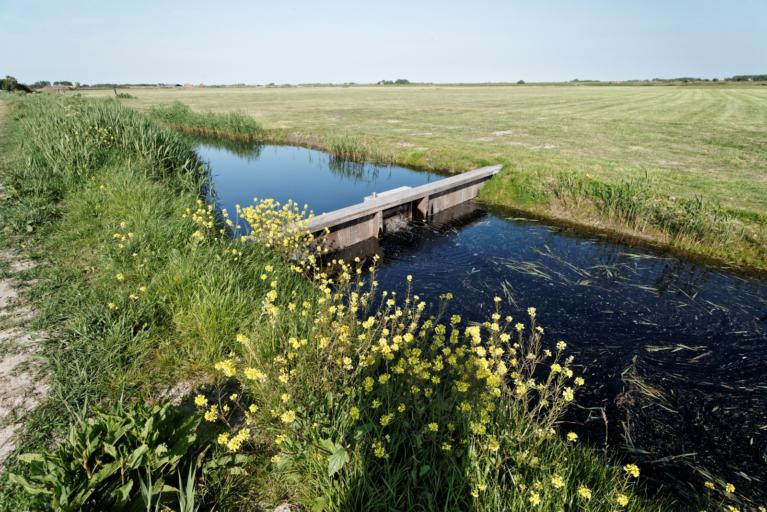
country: NL
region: North Holland
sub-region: Gemeente Den Helder
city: Den Helder
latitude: 53.0148
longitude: 4.7489
